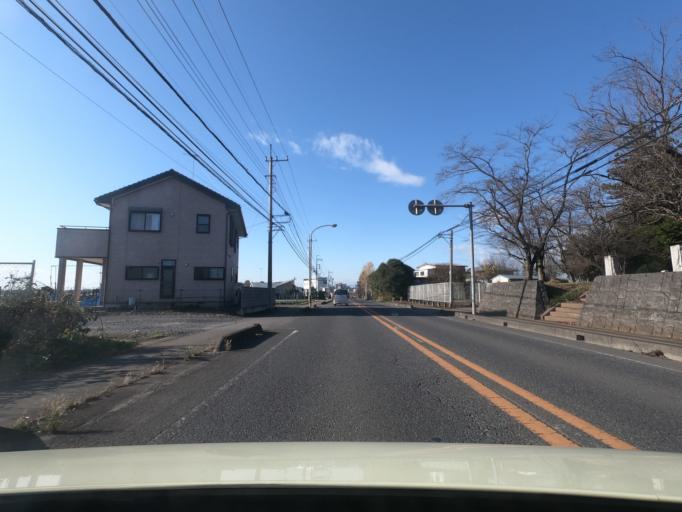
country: JP
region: Ibaraki
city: Koga
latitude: 36.2062
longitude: 139.7743
